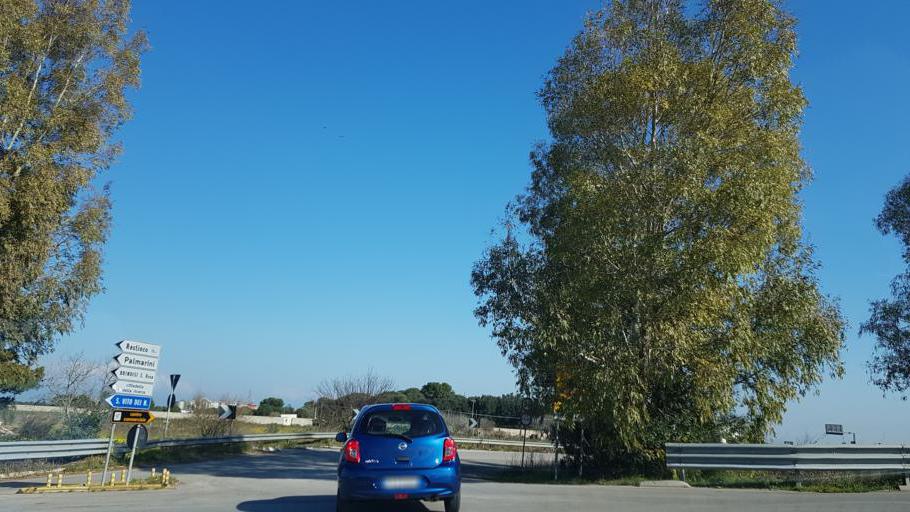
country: IT
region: Apulia
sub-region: Provincia di Brindisi
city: Brindisi
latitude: 40.6052
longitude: 17.8818
